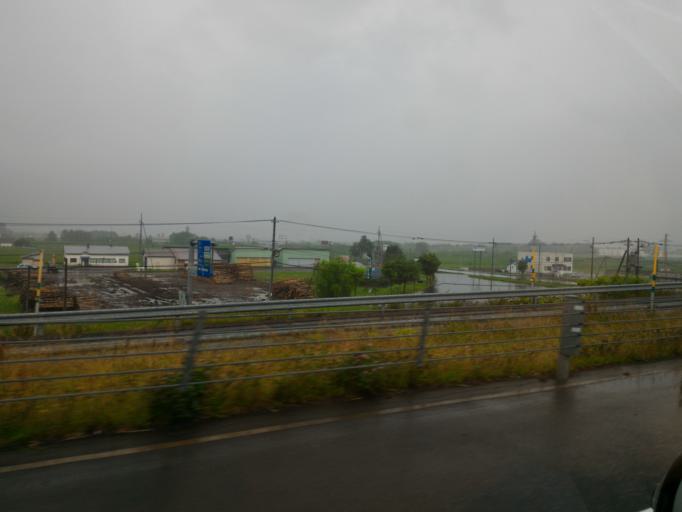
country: JP
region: Hokkaido
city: Nayoro
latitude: 44.3626
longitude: 142.4358
